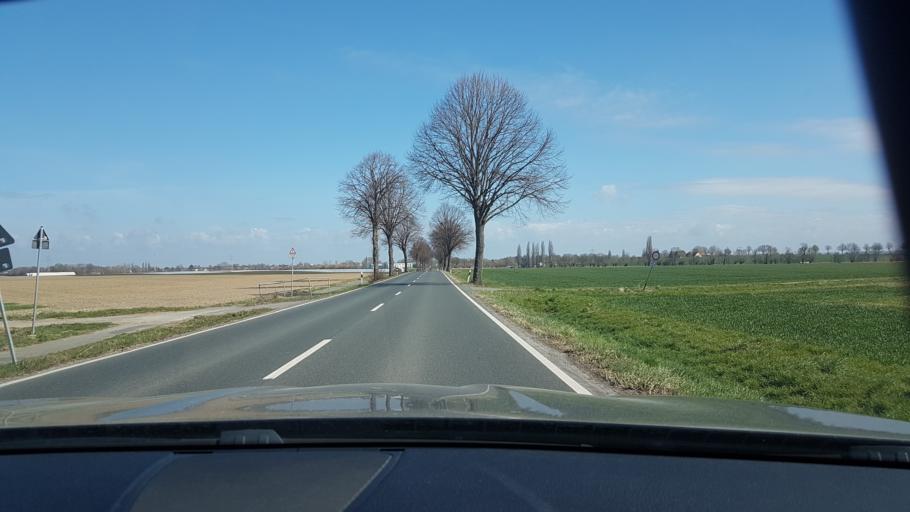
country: DE
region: Lower Saxony
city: Pattensen
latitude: 52.2477
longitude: 9.7416
